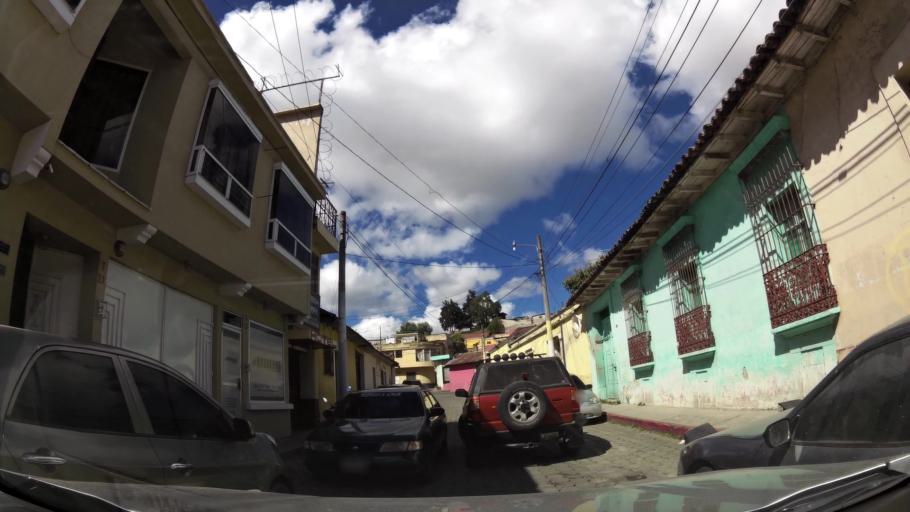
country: GT
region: Quetzaltenango
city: Quetzaltenango
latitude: 14.8345
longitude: -91.5153
